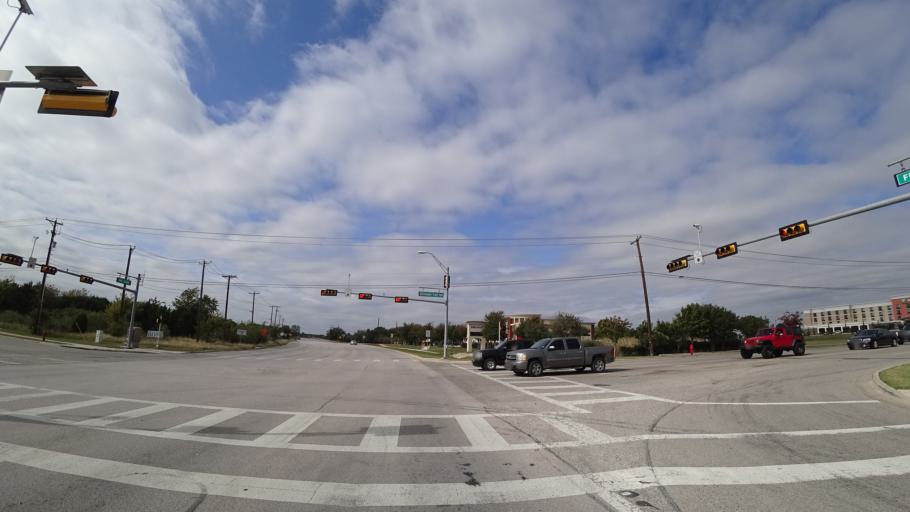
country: US
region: Texas
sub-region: Williamson County
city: Round Rock
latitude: 30.5361
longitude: -97.6948
